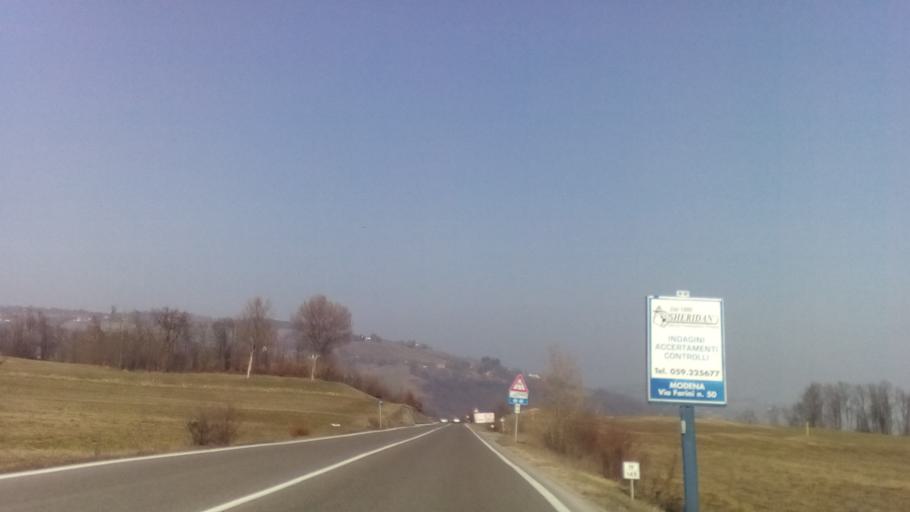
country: IT
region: Emilia-Romagna
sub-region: Provincia di Modena
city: Sant'Antonio
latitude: 44.3920
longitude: 10.8193
